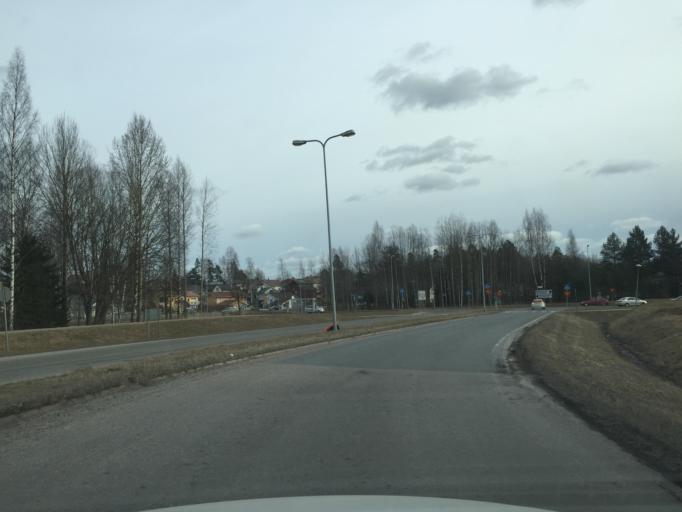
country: FI
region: Uusimaa
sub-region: Helsinki
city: Teekkarikylae
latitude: 60.2791
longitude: 24.8701
